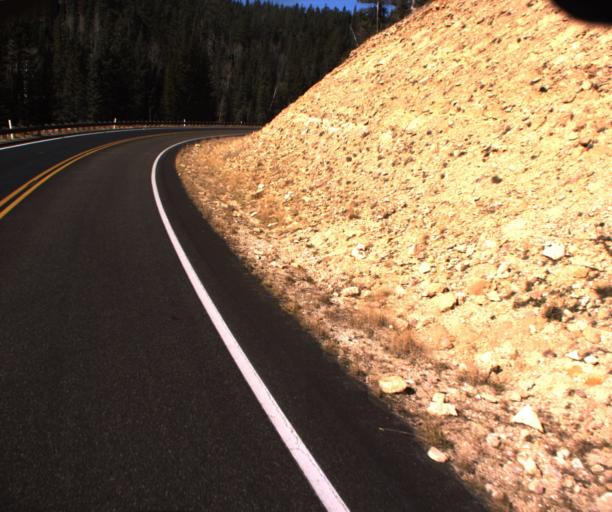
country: US
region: Arizona
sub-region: Coconino County
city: Grand Canyon
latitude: 36.5153
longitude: -112.1403
